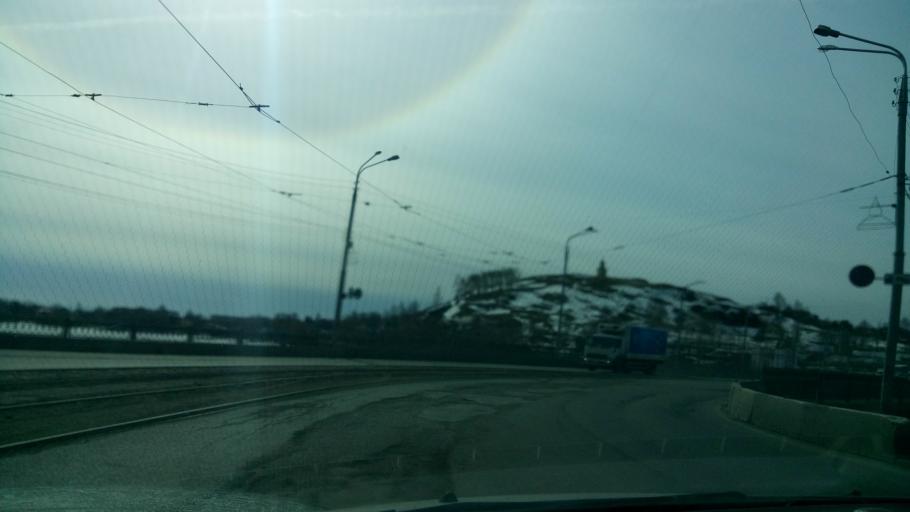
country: RU
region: Sverdlovsk
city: Nizhniy Tagil
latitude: 57.9046
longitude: 59.9499
